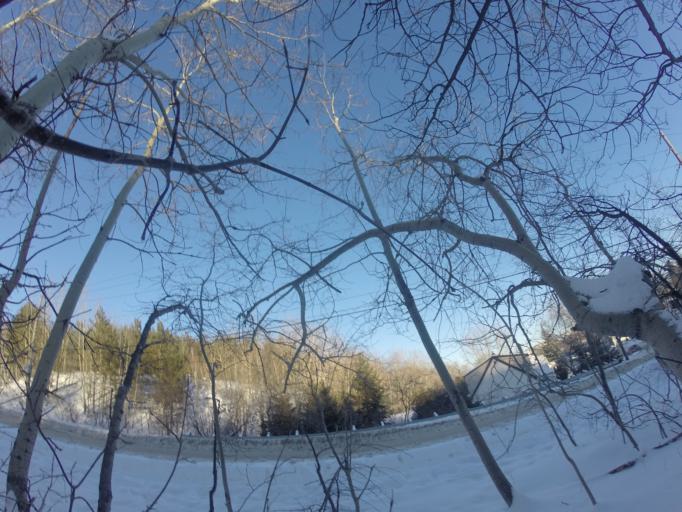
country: CA
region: Ontario
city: Greater Sudbury
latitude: 46.5062
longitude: -80.9982
